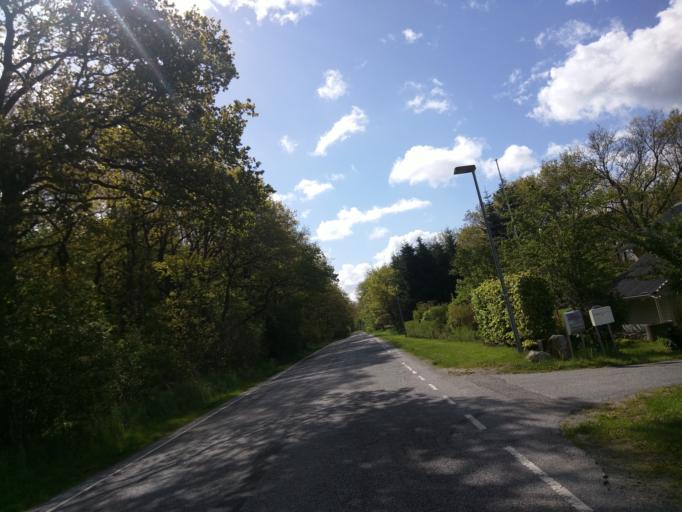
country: DK
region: Central Jutland
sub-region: Viborg Kommune
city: Viborg
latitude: 56.4106
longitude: 9.4200
